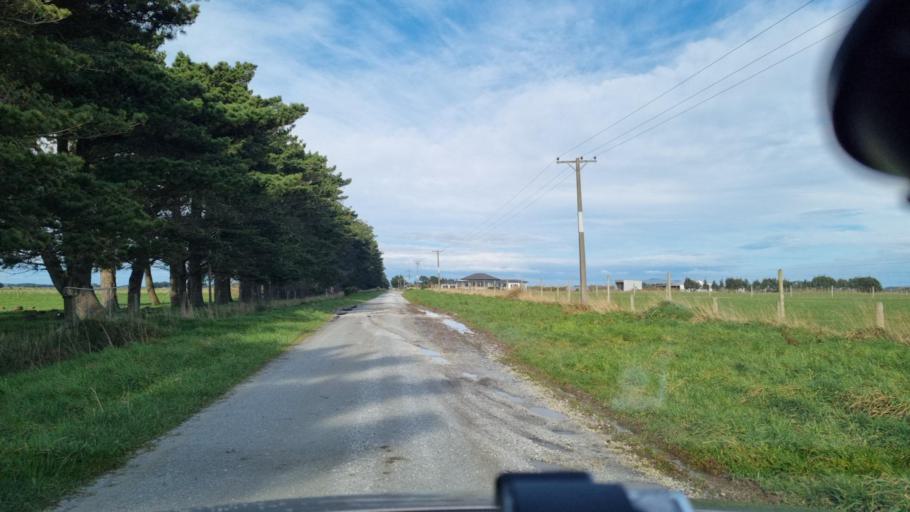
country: NZ
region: Southland
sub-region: Invercargill City
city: Invercargill
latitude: -46.4751
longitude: 168.4206
